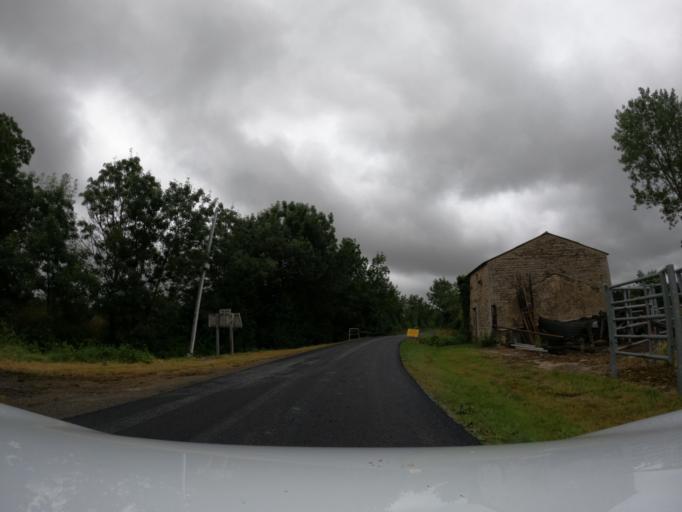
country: FR
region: Pays de la Loire
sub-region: Departement de la Vendee
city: Maillezais
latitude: 46.4017
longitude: -0.7441
